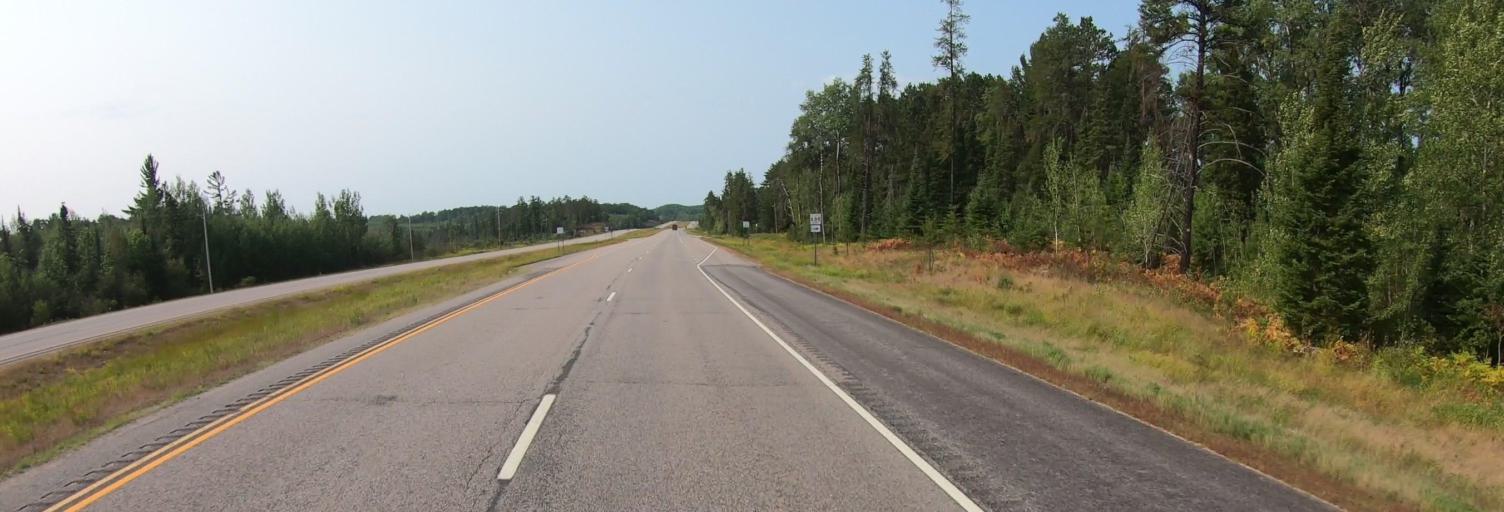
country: US
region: Minnesota
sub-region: Saint Louis County
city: Mountain Iron
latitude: 47.7010
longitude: -92.6449
